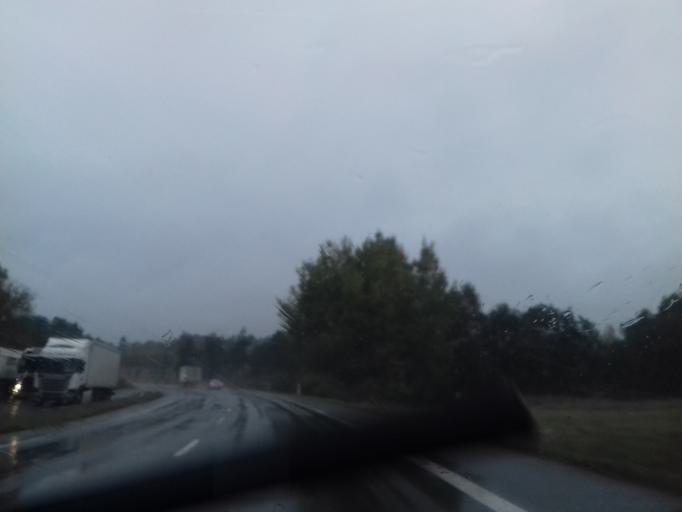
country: CZ
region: Pardubicky
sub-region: Okres Svitavy
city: Svitavy
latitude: 49.8035
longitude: 16.4571
